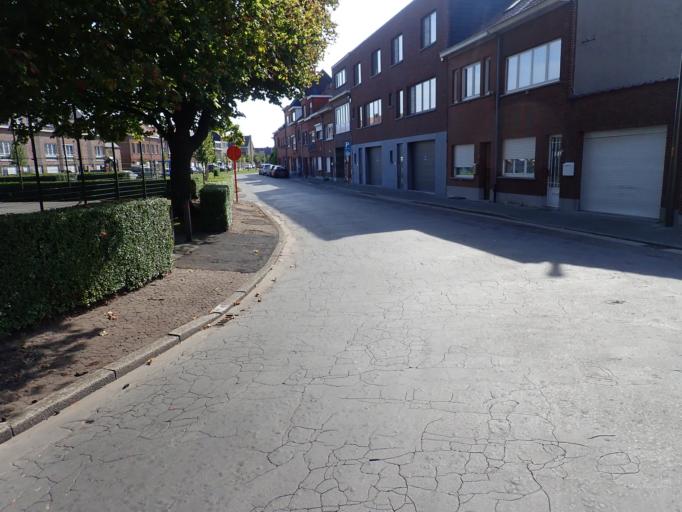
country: BE
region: Flanders
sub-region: Provincie Antwerpen
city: Mechelen
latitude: 51.0164
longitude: 4.4941
